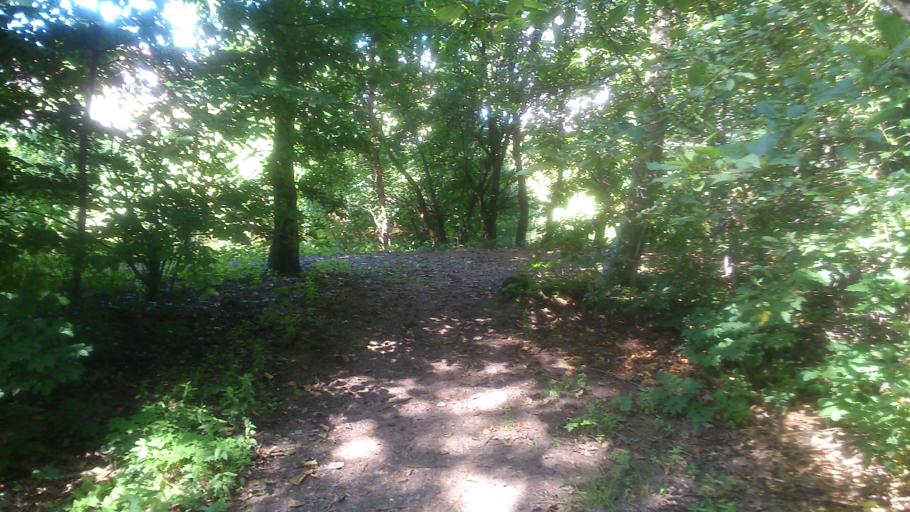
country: DK
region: Central Jutland
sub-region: Ringkobing-Skjern Kommune
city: Skjern
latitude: 56.0213
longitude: 8.5342
